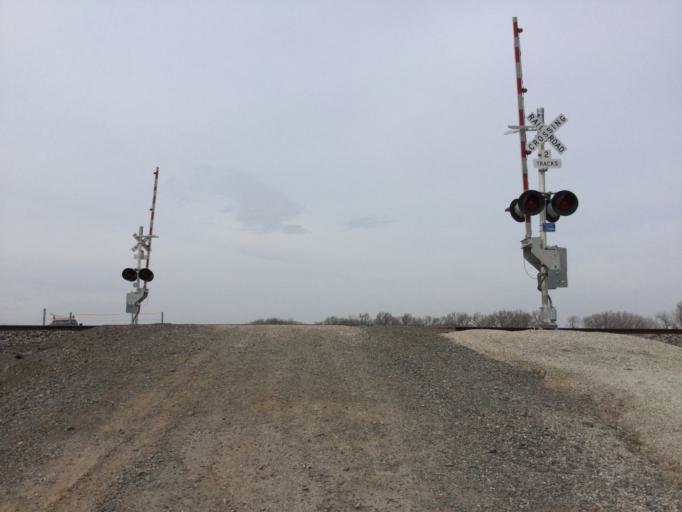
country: US
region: Kansas
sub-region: Barber County
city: Kiowa
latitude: 37.1230
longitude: -98.3703
